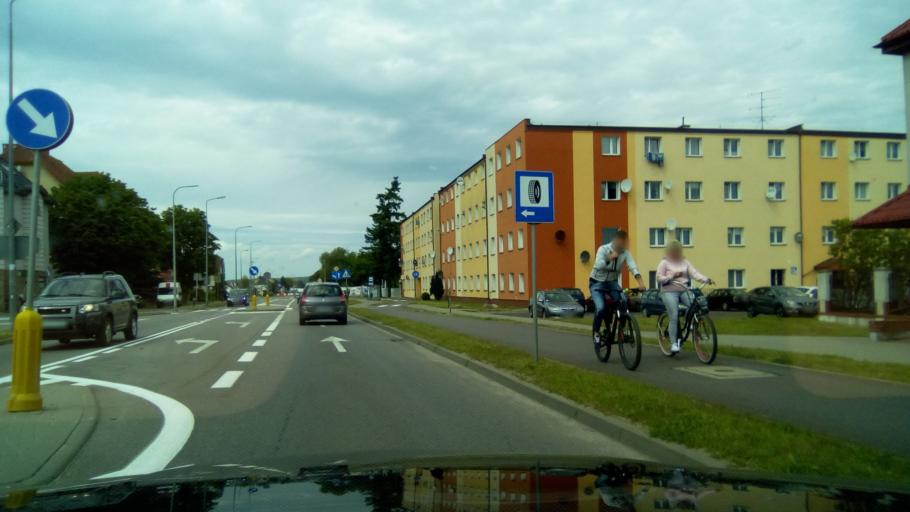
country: PL
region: Pomeranian Voivodeship
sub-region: Powiat leborski
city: Lebork
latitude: 54.5304
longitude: 17.7624
